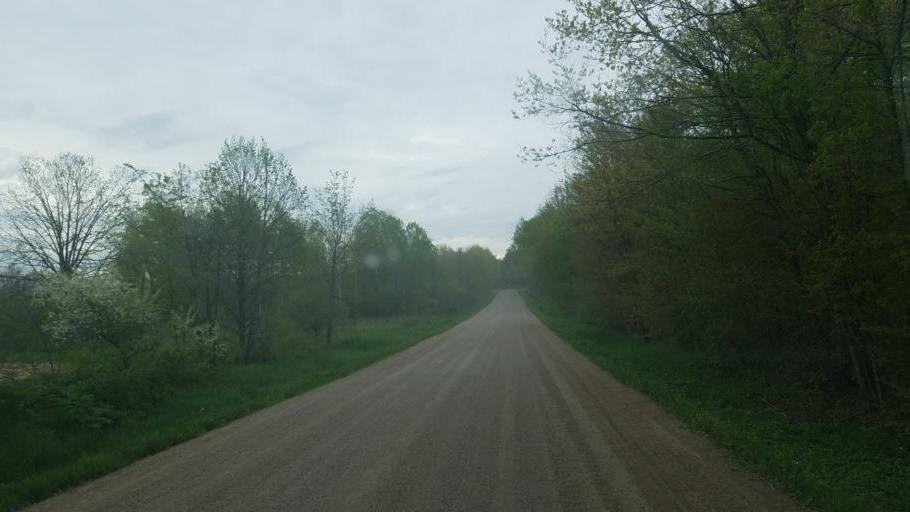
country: US
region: Wisconsin
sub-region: Clark County
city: Loyal
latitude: 44.6327
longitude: -90.4409
